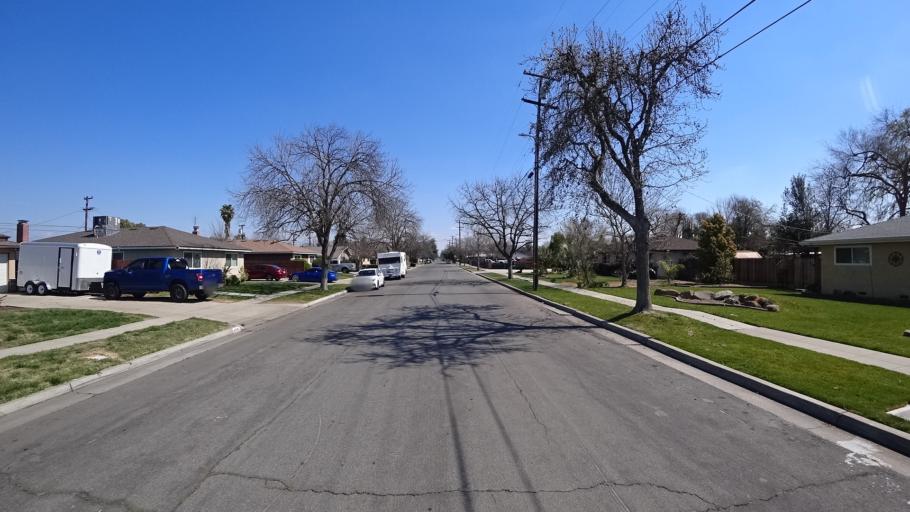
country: US
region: California
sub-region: Fresno County
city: Tarpey Village
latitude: 36.7977
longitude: -119.7385
